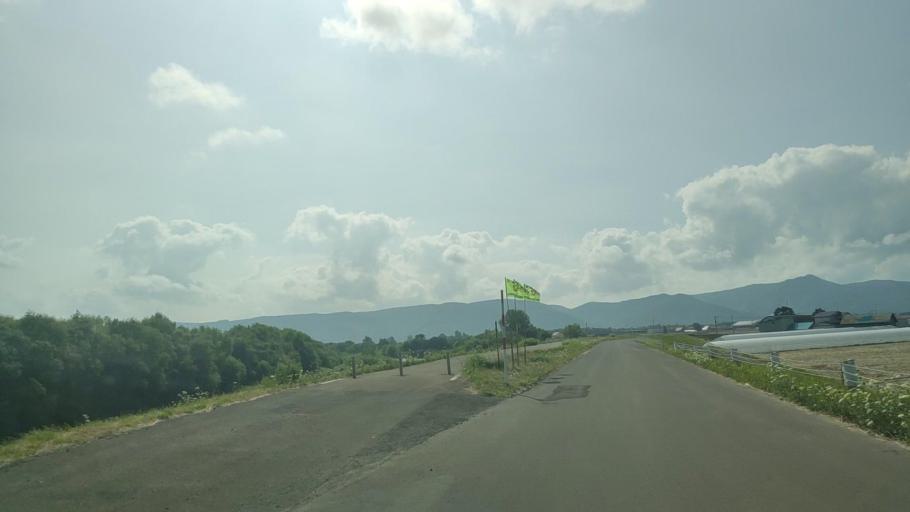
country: JP
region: Hokkaido
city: Shimo-furano
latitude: 43.3397
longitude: 142.3762
